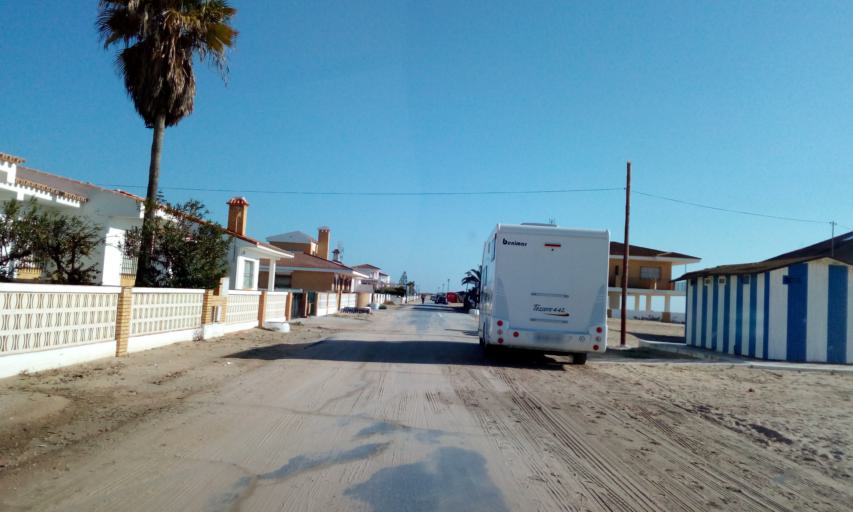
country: ES
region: Andalusia
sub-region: Provincia de Huelva
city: Lepe
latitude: 37.2062
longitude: -7.2011
